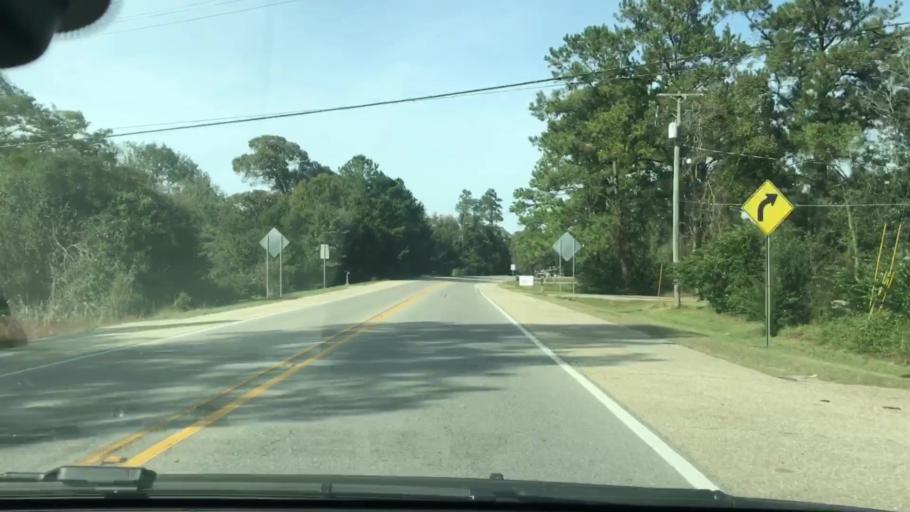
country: US
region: Louisiana
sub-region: Saint Tammany Parish
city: Pearl River
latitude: 30.4171
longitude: -89.7855
